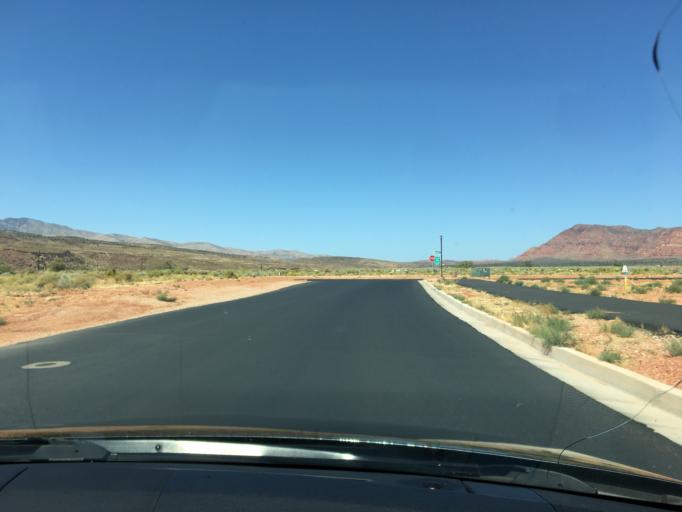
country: US
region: Utah
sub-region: Washington County
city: Ivins
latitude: 37.1611
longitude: -113.6932
